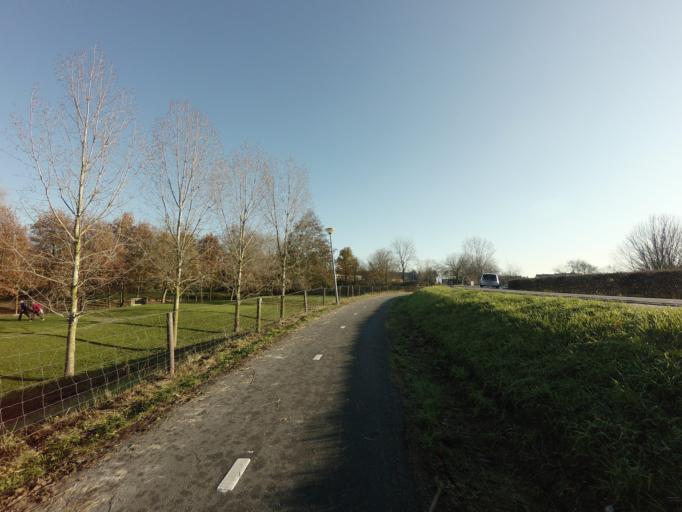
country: NL
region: Gelderland
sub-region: Gemeente Maasdriel
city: Heerewaarden
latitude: 51.7769
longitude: 5.3318
